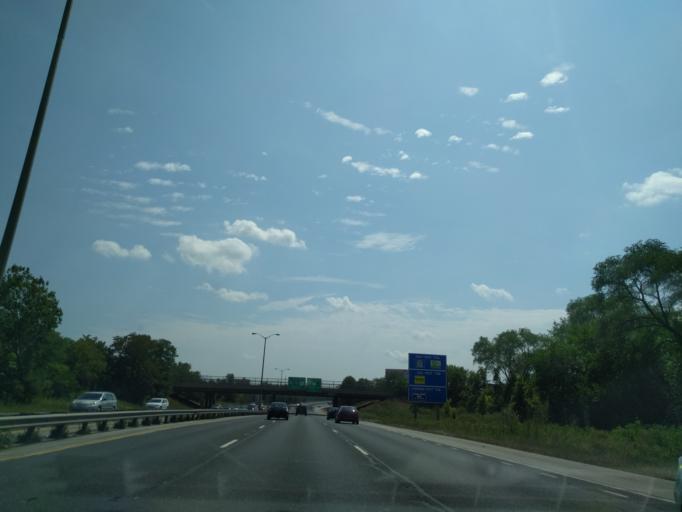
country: US
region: Illinois
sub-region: Cook County
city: Burnham
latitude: 41.6168
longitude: -87.5790
